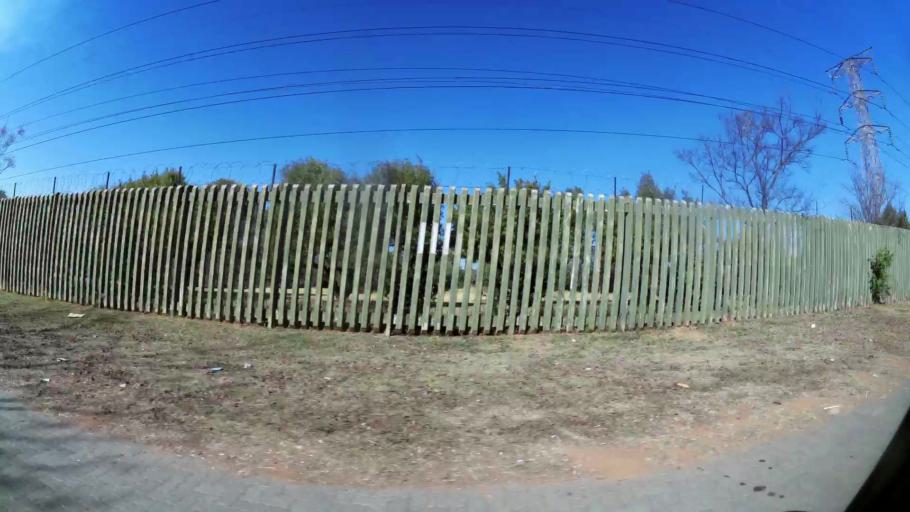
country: ZA
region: Gauteng
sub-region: City of Johannesburg Metropolitan Municipality
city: Roodepoort
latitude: -26.1020
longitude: 27.9641
